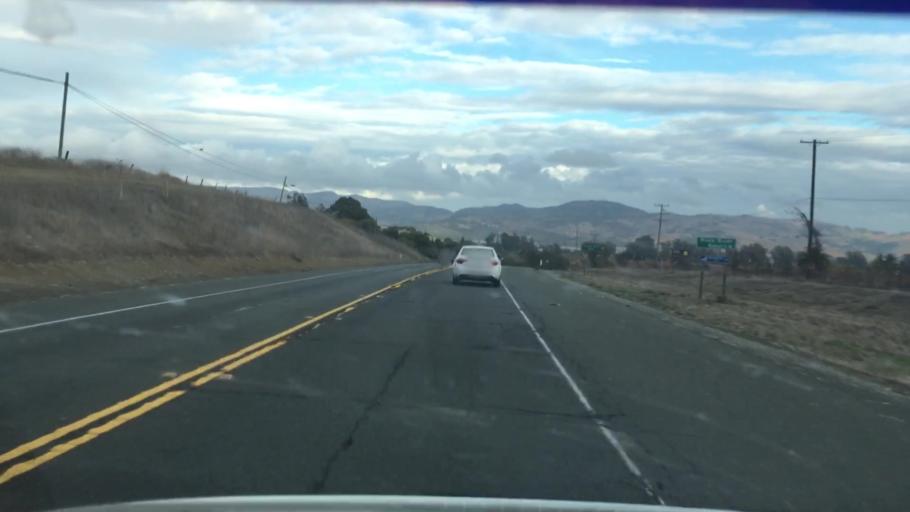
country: US
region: California
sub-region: Napa County
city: Napa
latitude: 38.2556
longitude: -122.3303
